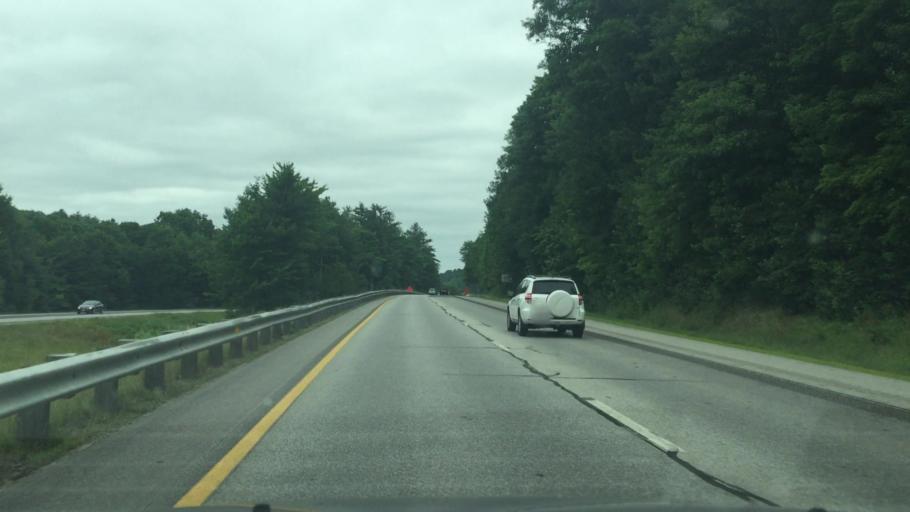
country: US
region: New Hampshire
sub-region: Merrimack County
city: Northfield
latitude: 43.4114
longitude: -71.5956
